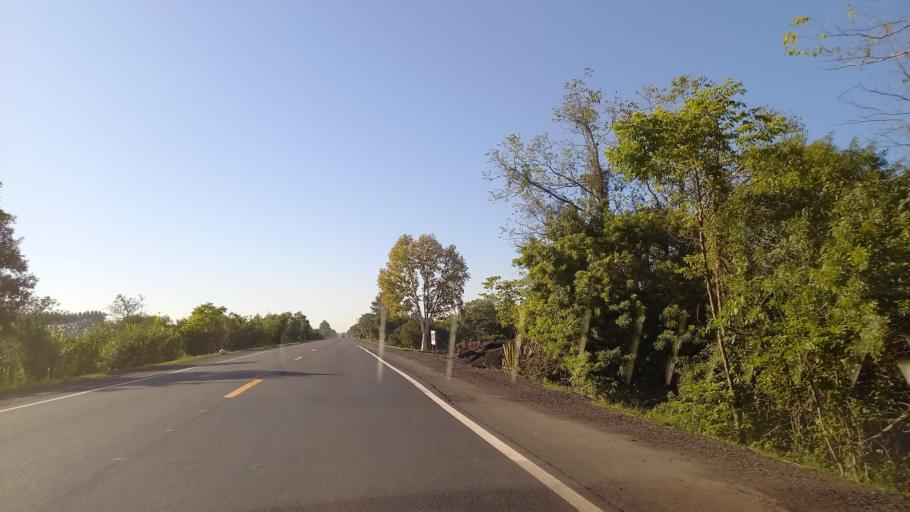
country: BR
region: Rio Grande do Sul
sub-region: Venancio Aires
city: Venancio Aires
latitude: -29.6592
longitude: -52.0762
